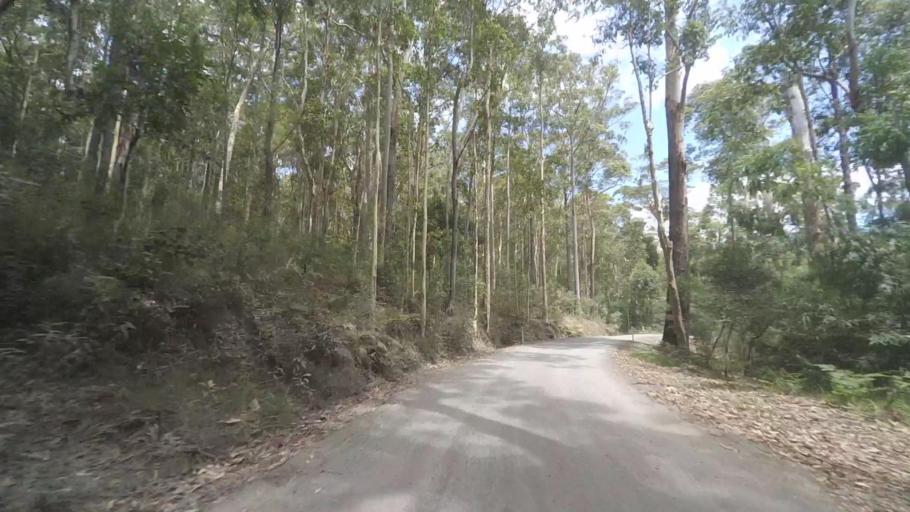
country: AU
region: New South Wales
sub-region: Shoalhaven Shire
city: Milton
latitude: -35.4381
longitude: 150.3215
